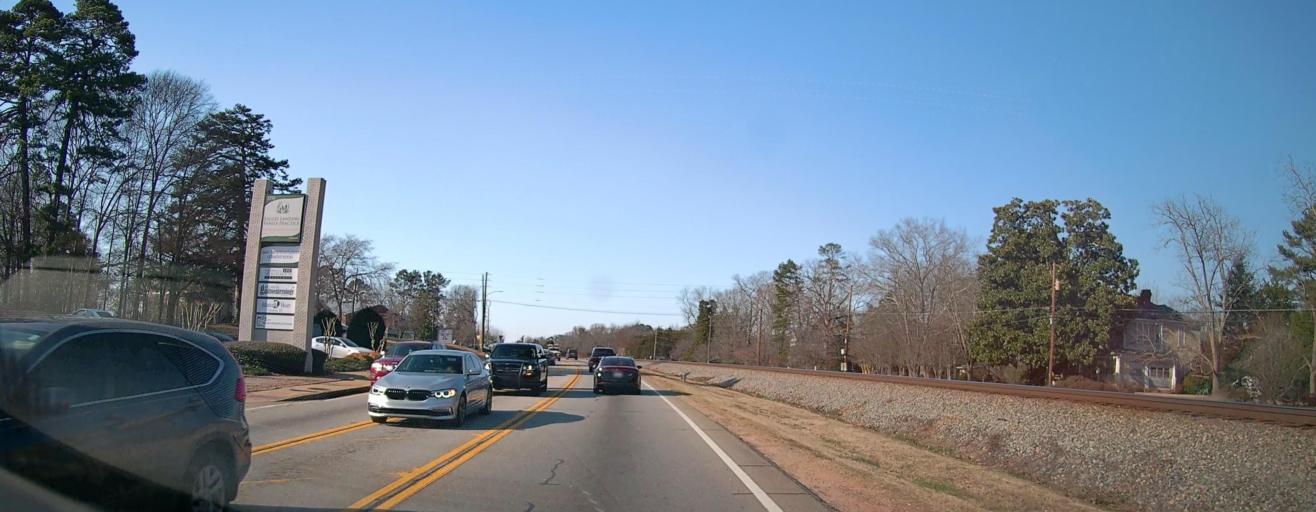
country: US
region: Georgia
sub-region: Henry County
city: Locust Grove
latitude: 33.3501
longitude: -84.1109
